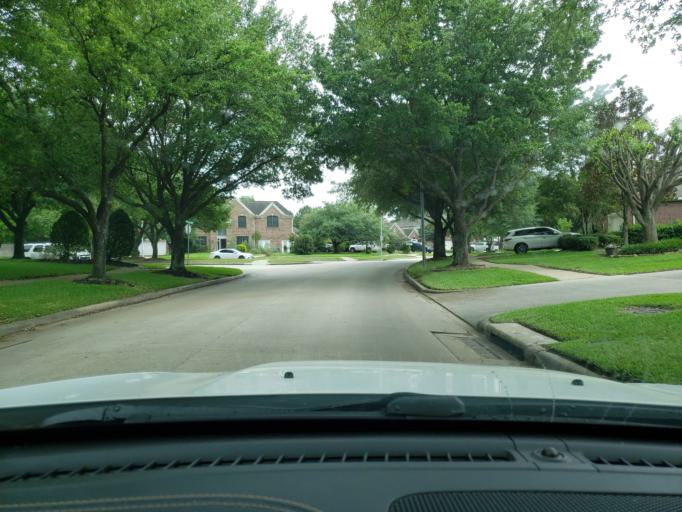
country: US
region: Texas
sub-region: Harris County
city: Jersey Village
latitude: 29.9205
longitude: -95.5642
